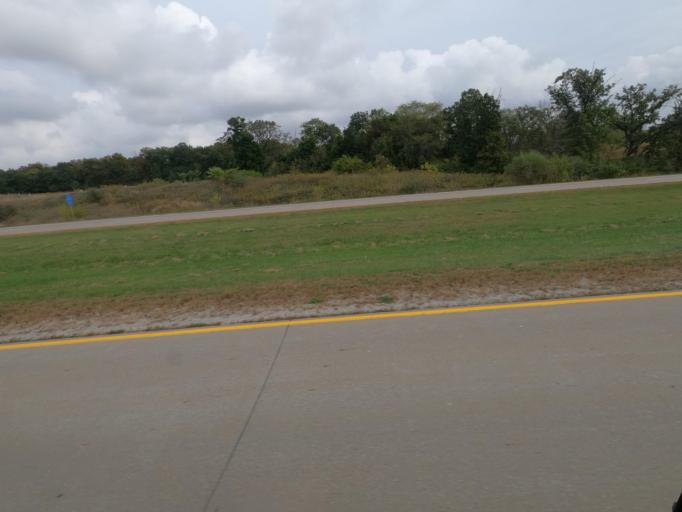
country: US
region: Iowa
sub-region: Wapello County
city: Ottumwa
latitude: 41.0452
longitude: -92.3727
